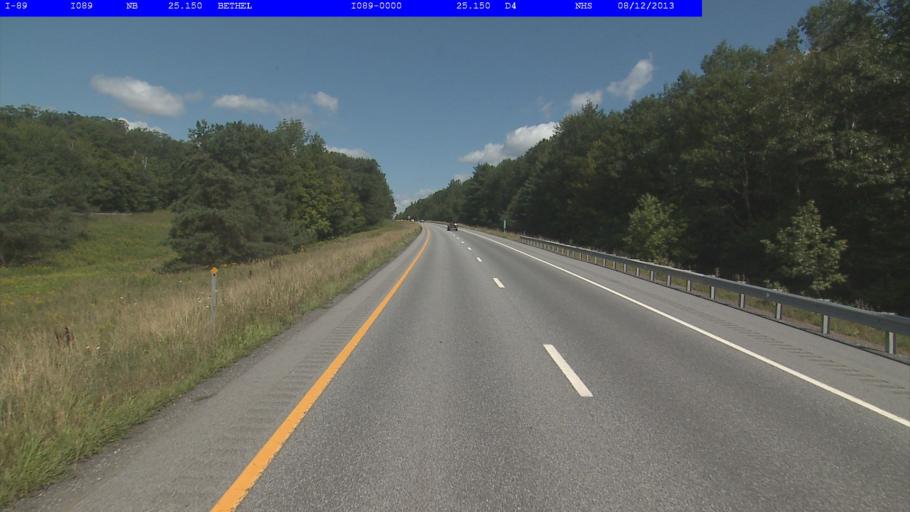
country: US
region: Vermont
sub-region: Orange County
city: Randolph
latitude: 43.8635
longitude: -72.6075
